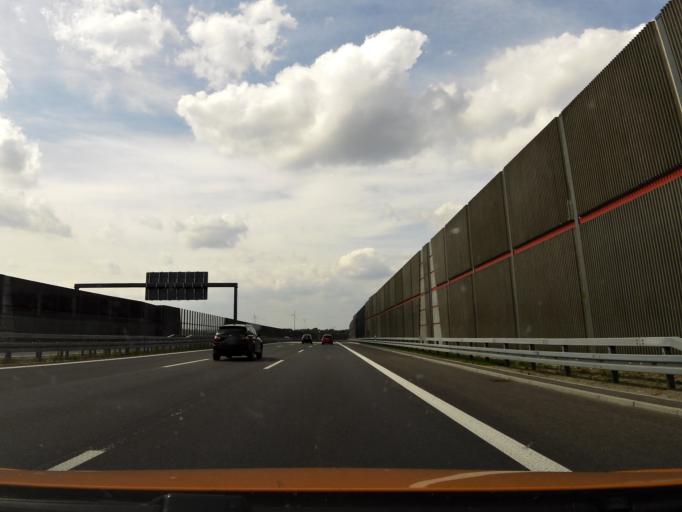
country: DE
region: Berlin
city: Buch
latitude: 52.6226
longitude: 13.4940
